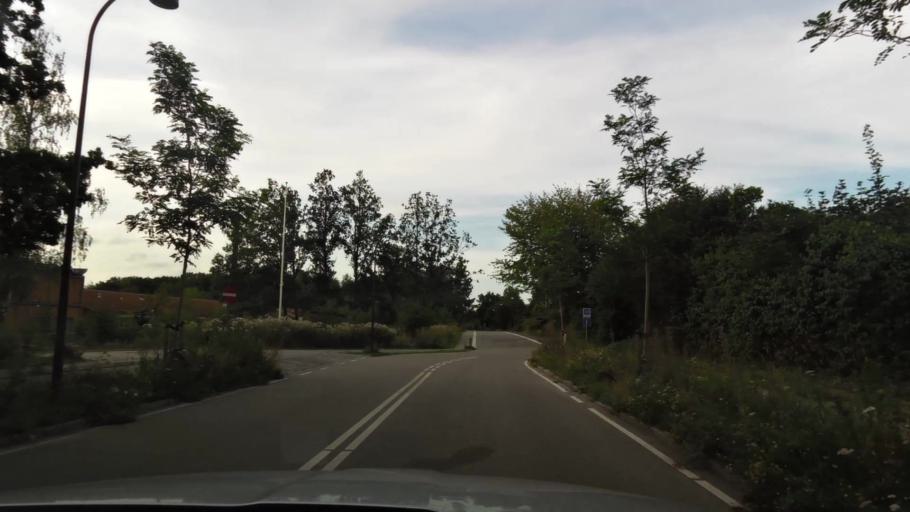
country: DK
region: Capital Region
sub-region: Rudersdal Kommune
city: Birkerod
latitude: 55.8400
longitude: 12.4155
